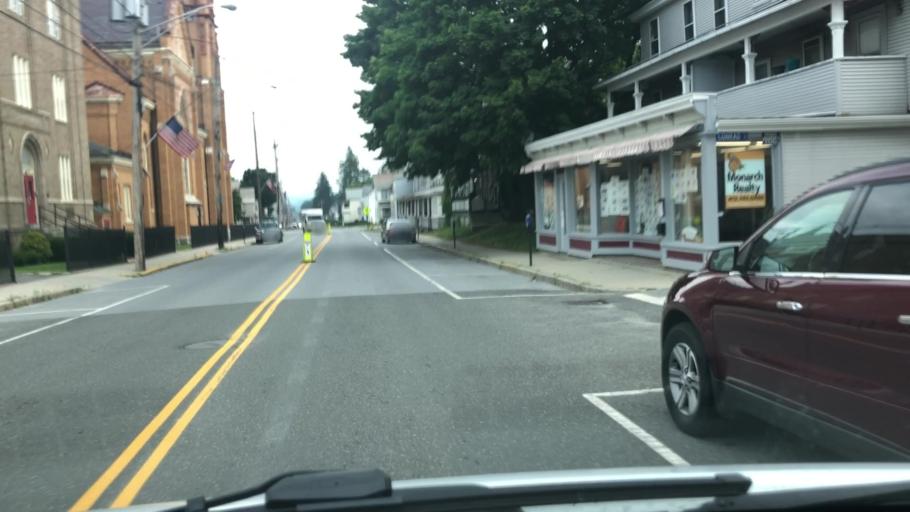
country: US
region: Massachusetts
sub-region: Berkshire County
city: Adams
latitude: 42.6241
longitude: -73.1135
